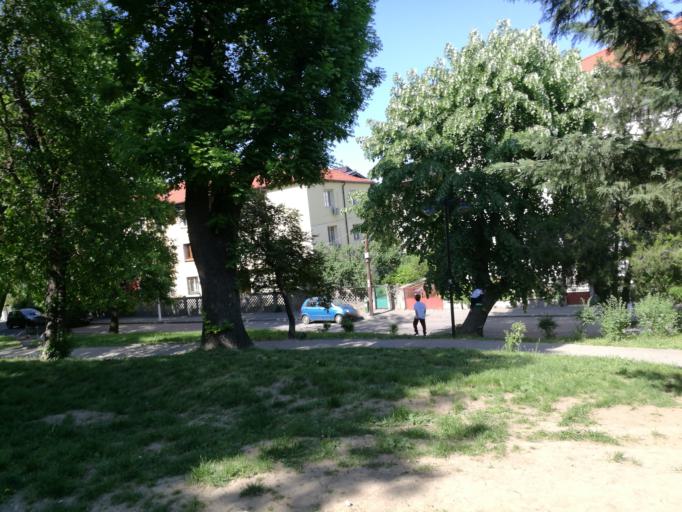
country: RO
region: Bucuresti
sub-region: Municipiul Bucuresti
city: Bucuresti
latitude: 44.4286
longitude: 26.0689
